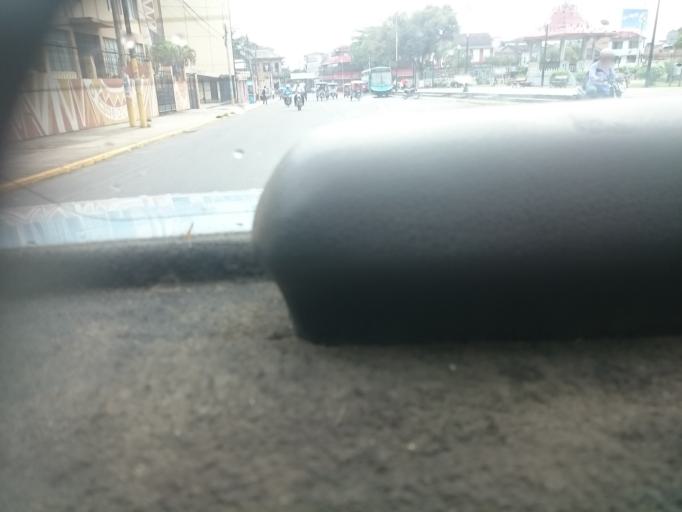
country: PE
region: Loreto
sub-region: Provincia de Maynas
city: Iquitos
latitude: -3.7543
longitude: -73.2498
